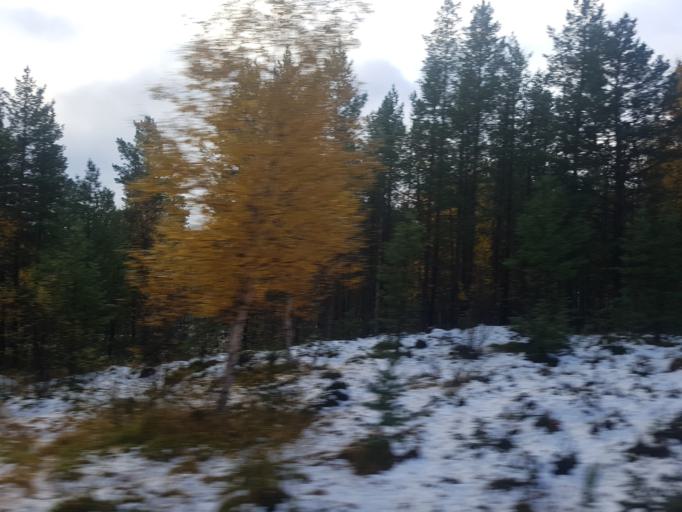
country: NO
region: Sor-Trondelag
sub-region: Oppdal
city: Oppdal
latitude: 62.6334
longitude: 9.7942
